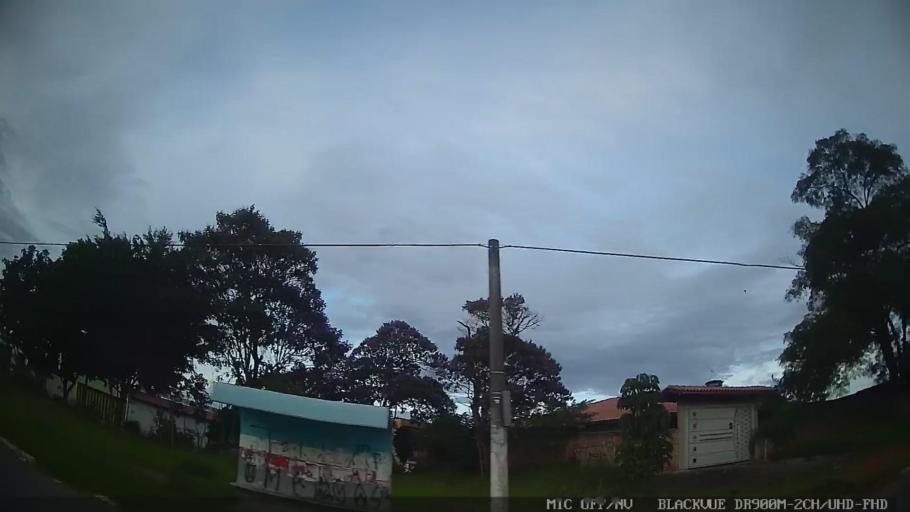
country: BR
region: Sao Paulo
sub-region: Suzano
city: Suzano
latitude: -23.5036
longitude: -46.3084
